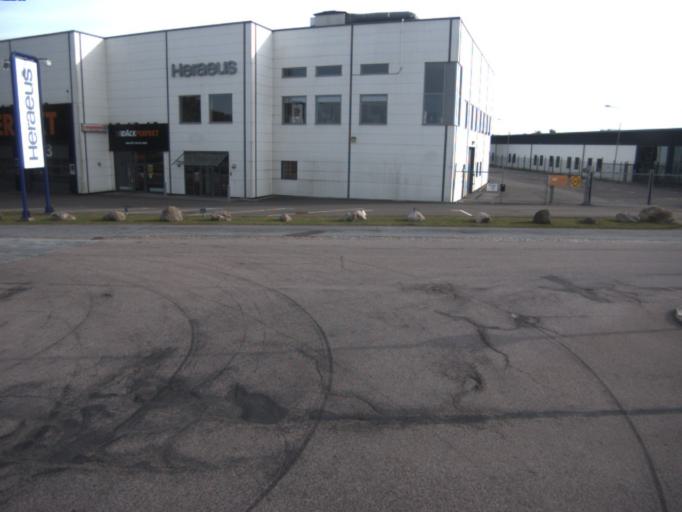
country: SE
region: Skane
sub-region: Helsingborg
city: Odakra
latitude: 56.0777
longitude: 12.7273
